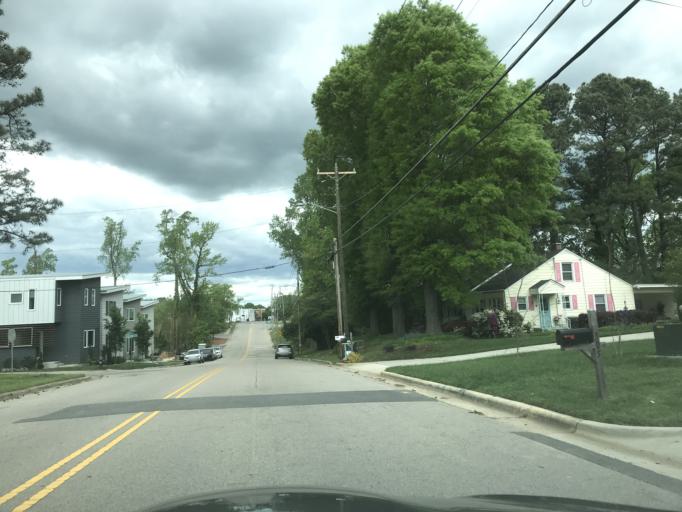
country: US
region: North Carolina
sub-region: Wake County
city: West Raleigh
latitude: 35.7884
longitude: -78.7131
